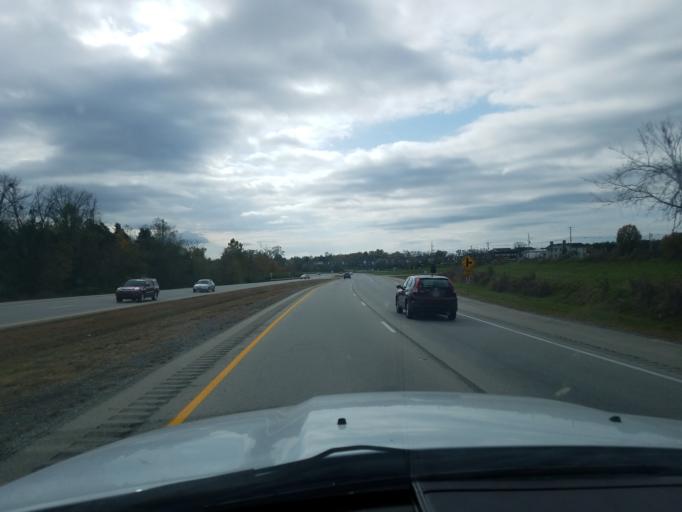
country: US
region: Kentucky
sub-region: Bullitt County
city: Mount Washington
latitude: 38.1024
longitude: -85.5656
